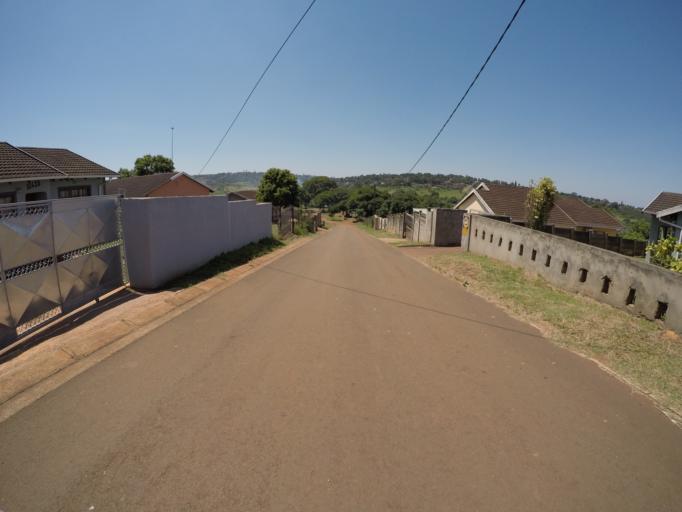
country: ZA
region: KwaZulu-Natal
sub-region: uThungulu District Municipality
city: Empangeni
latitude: -28.7718
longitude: 31.8832
